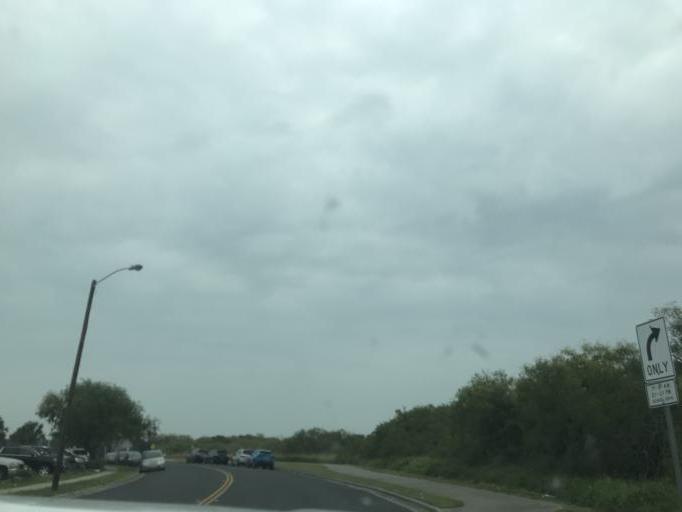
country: US
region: Texas
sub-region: Nueces County
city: Corpus Christi
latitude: 27.6681
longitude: -97.3488
